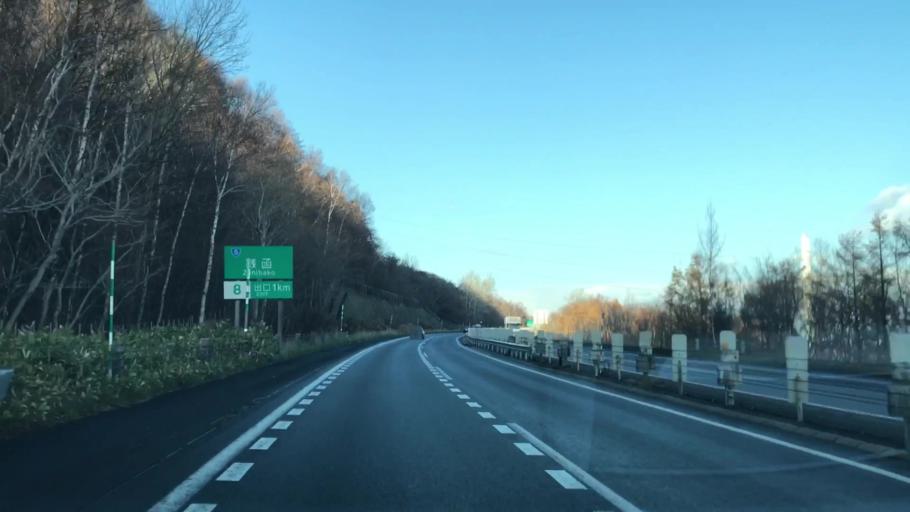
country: JP
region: Hokkaido
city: Sapporo
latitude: 43.1290
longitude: 141.1881
